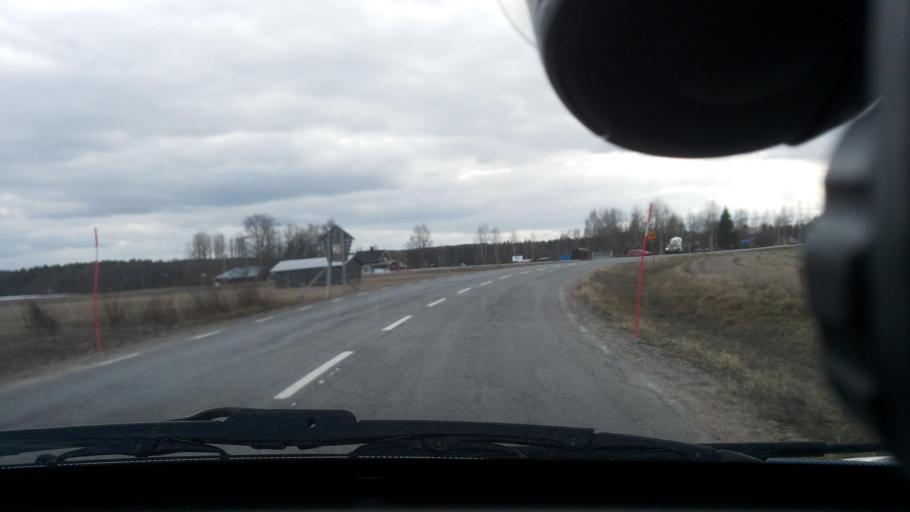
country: SE
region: Norrbotten
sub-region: Bodens Kommun
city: Saevast
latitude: 65.6767
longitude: 21.7995
